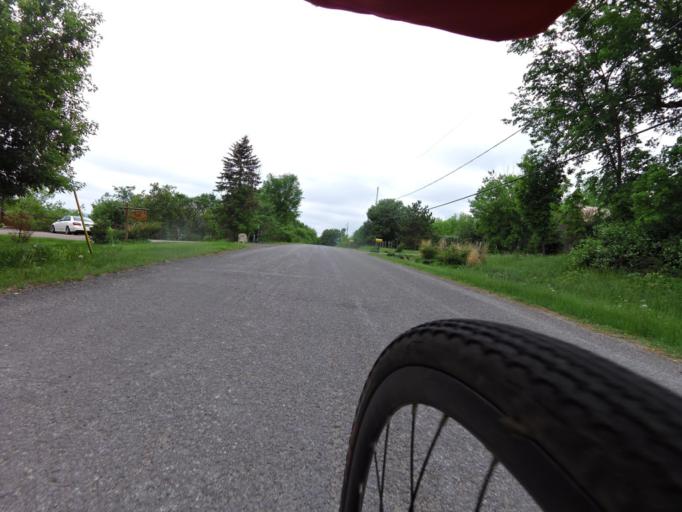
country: CA
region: Ontario
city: Renfrew
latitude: 45.2920
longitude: -76.7226
